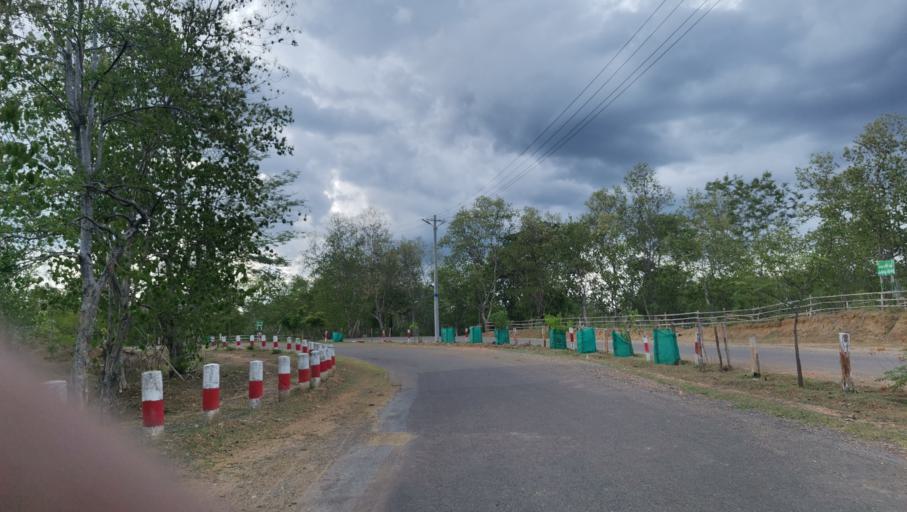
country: MM
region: Magway
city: Minbu
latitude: 20.0866
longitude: 94.5768
